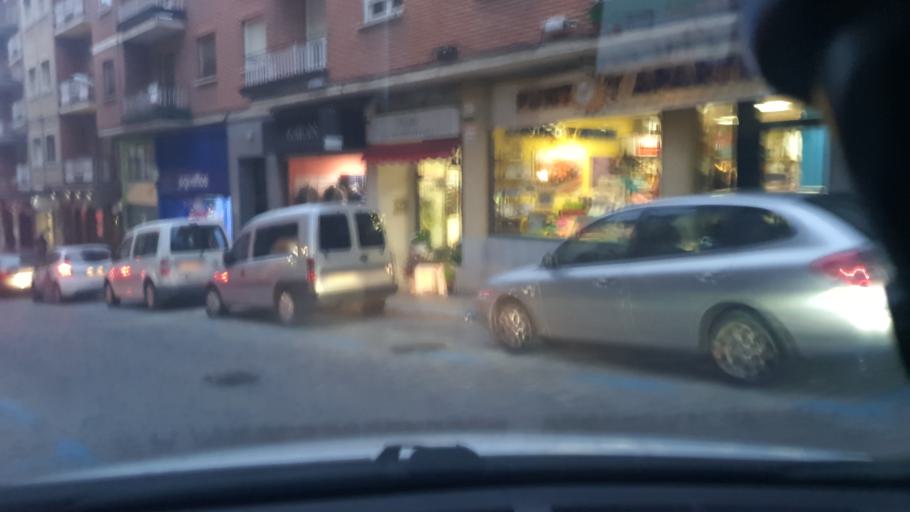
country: ES
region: Castille and Leon
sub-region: Provincia de Segovia
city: Segovia
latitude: 40.9448
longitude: -4.1181
